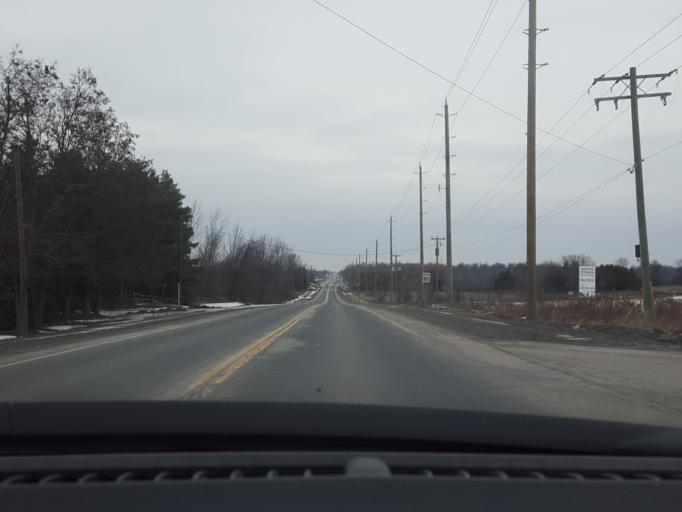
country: CA
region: Ontario
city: Keswick
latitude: 44.1820
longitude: -79.4354
